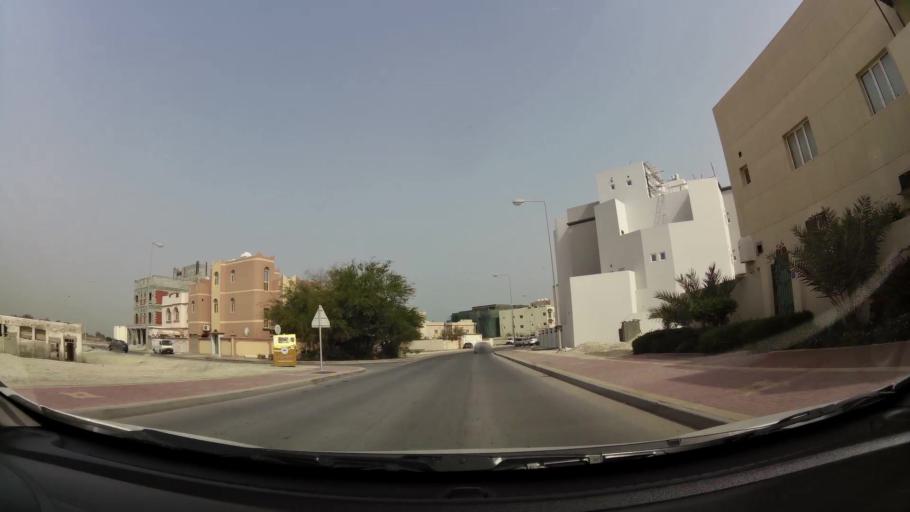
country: BH
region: Manama
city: Jidd Hafs
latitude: 26.2339
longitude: 50.5247
